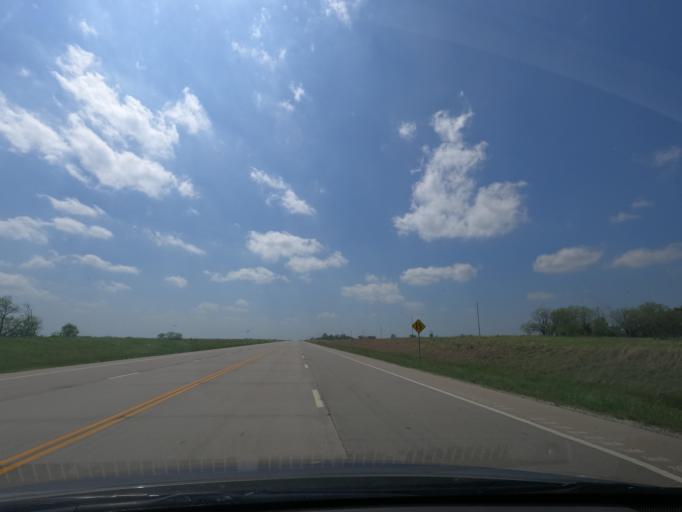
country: US
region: Kansas
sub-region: Elk County
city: Howard
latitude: 37.6347
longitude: -96.1879
